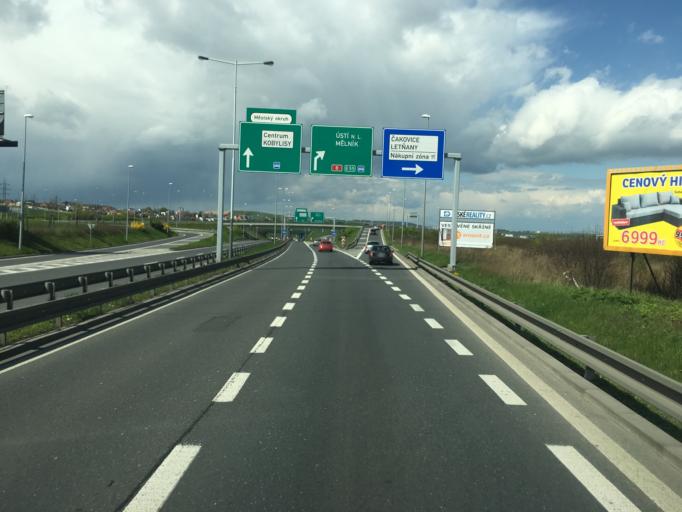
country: CZ
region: Praha
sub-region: Praha 9
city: Strizkov
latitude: 50.1345
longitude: 14.4967
